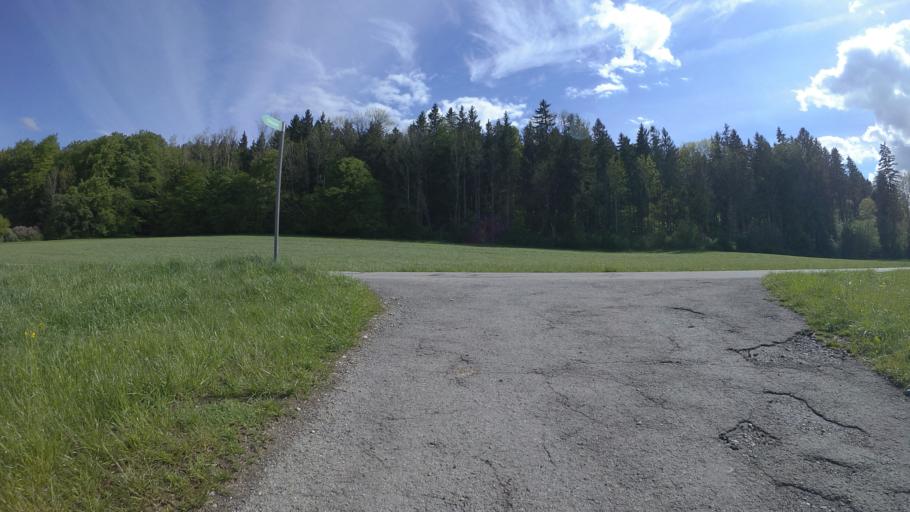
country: DE
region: Bavaria
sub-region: Upper Bavaria
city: Grabenstatt
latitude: 47.8431
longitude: 12.5666
